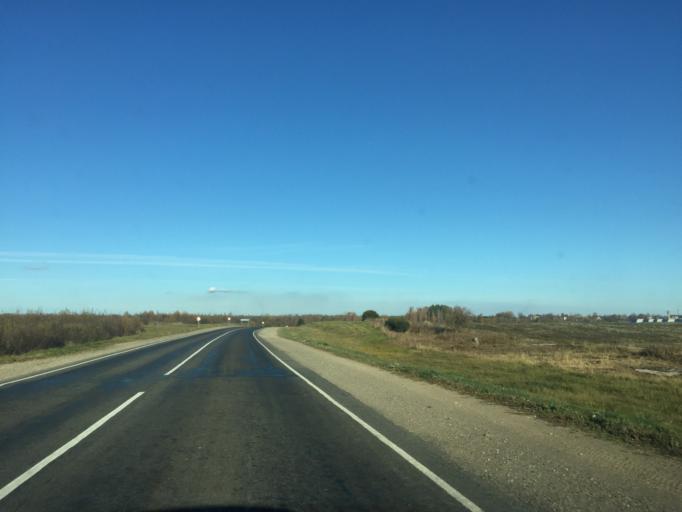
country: BY
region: Vitebsk
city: Dzisna
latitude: 55.3437
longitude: 28.2945
